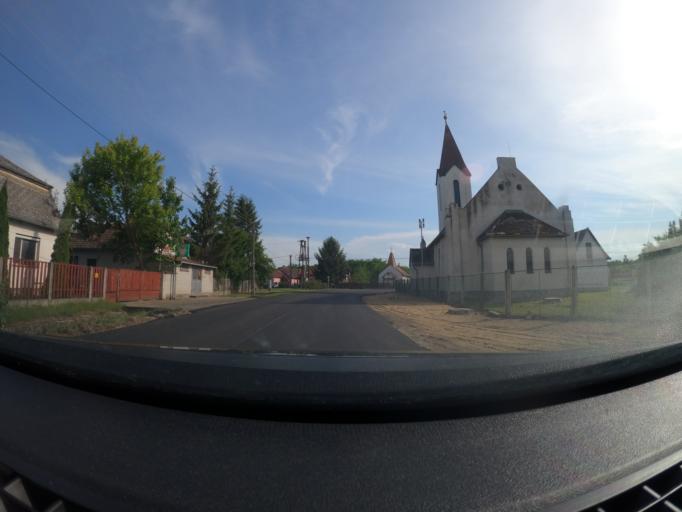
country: HU
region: Hajdu-Bihar
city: Nyirabrany
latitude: 47.5317
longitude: 21.9983
